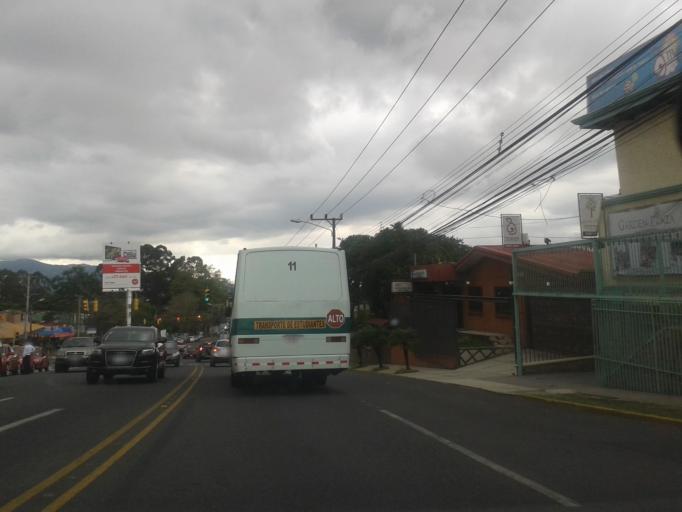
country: CR
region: San Jose
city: San Vicente de Moravia
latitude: 9.9633
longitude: -84.0563
